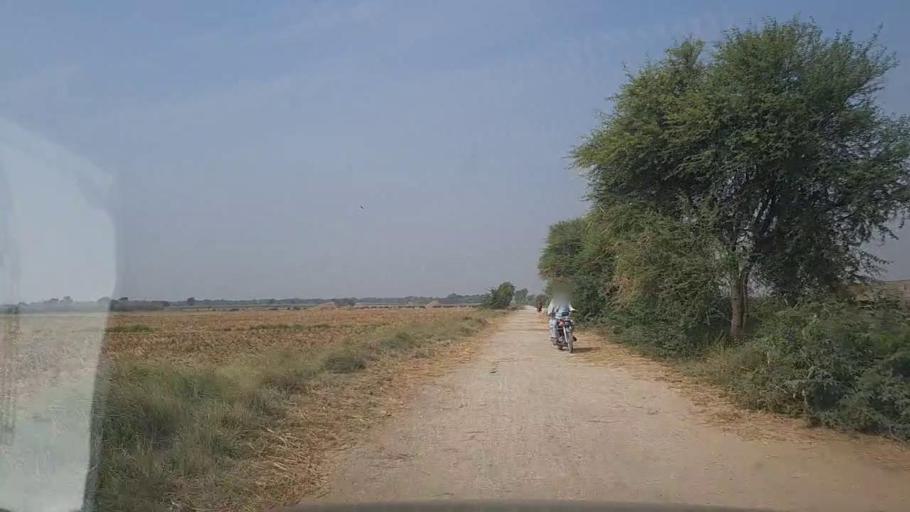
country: PK
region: Sindh
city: Bulri
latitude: 24.9731
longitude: 68.3070
